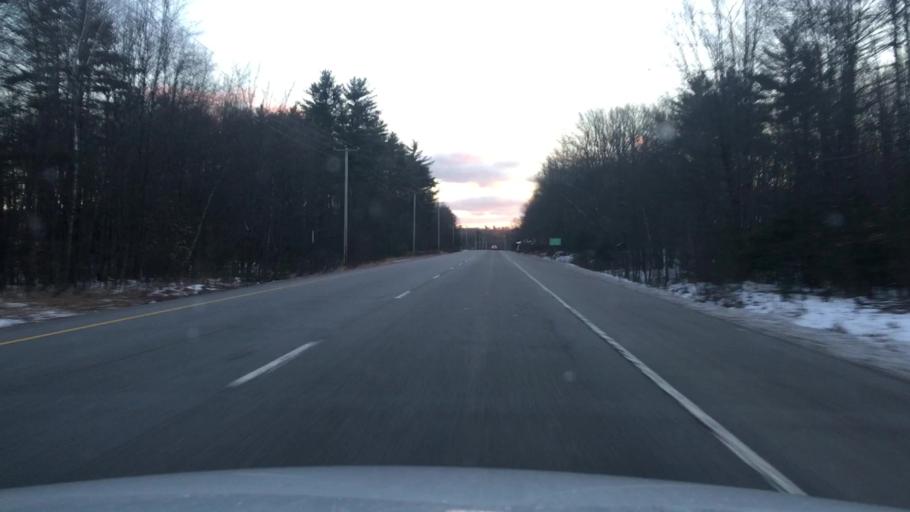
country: US
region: Maine
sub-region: Androscoggin County
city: Auburn
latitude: 44.0542
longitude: -70.2563
